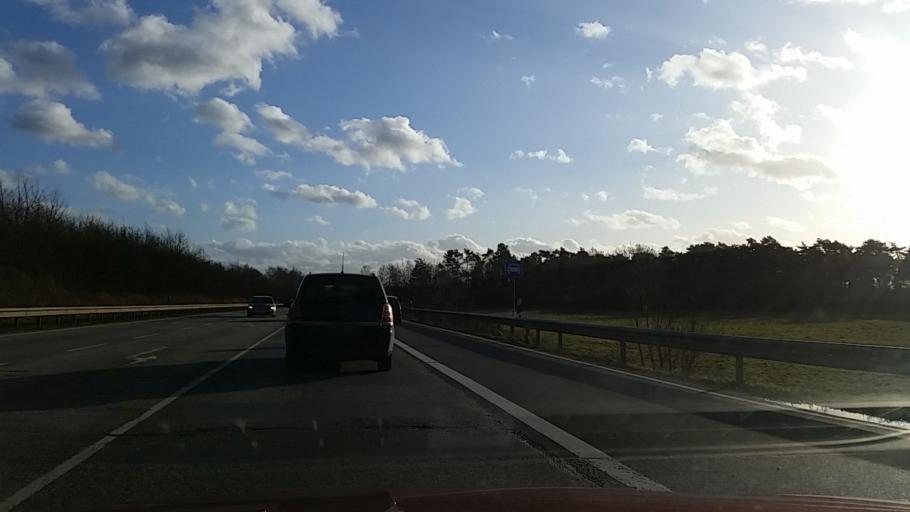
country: DE
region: Schleswig-Holstein
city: Glinde
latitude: 53.5574
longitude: 10.2309
